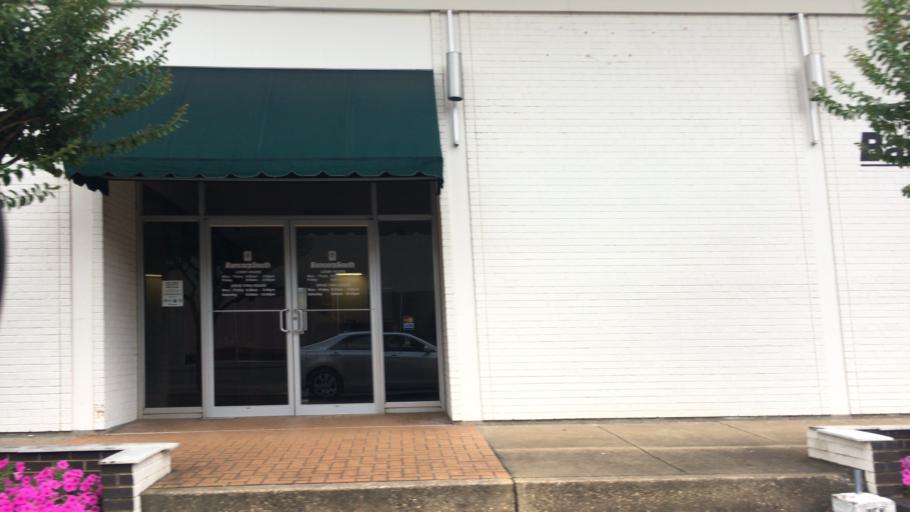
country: US
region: Louisiana
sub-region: Lincoln Parish
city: Ruston
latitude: 32.5308
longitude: -92.6391
